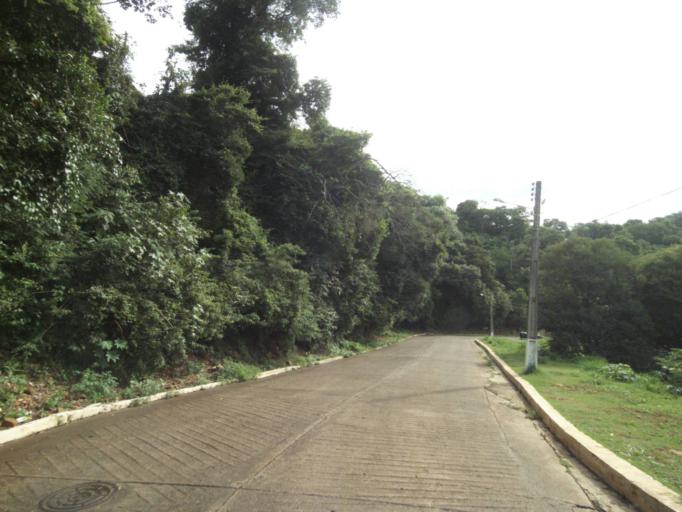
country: BR
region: Parana
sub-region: Guaraniacu
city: Guaraniacu
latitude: -25.1019
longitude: -52.8718
